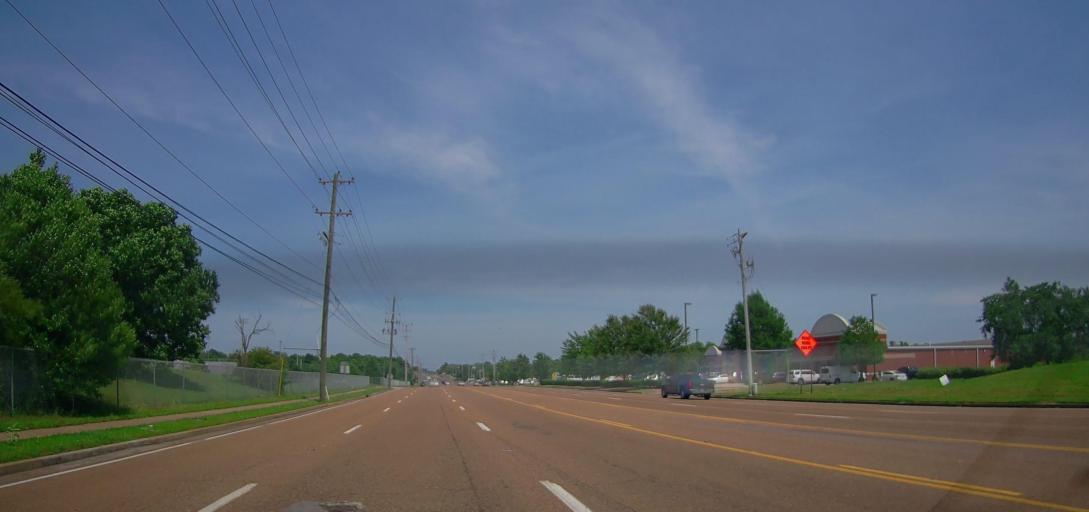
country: US
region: Mississippi
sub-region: De Soto County
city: Olive Branch
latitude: 35.0205
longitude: -89.8004
